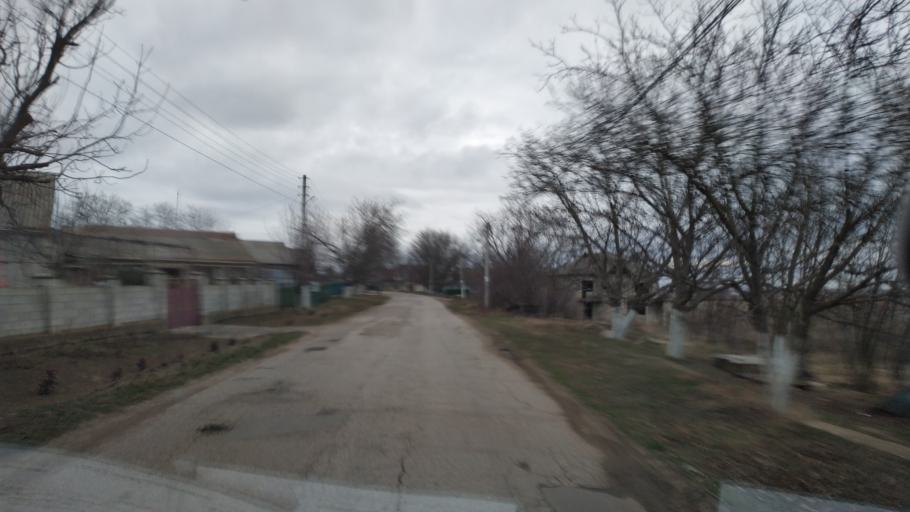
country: MD
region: Bender
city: Bender
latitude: 46.7727
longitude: 29.4832
